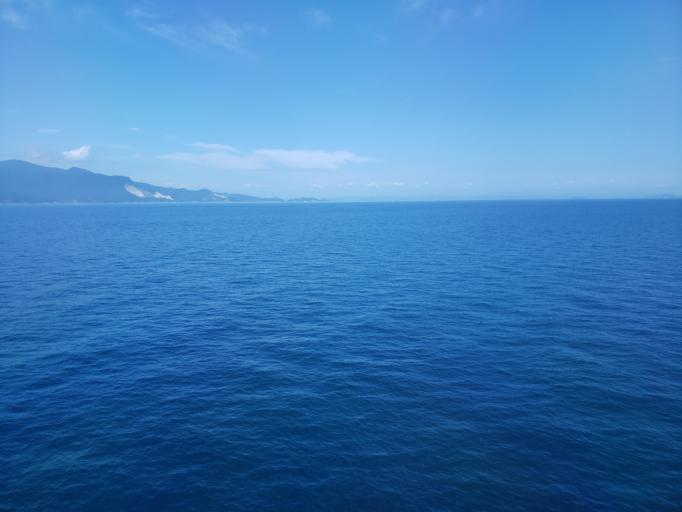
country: JP
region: Kagawa
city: Tonosho
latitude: 34.4468
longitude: 134.4199
